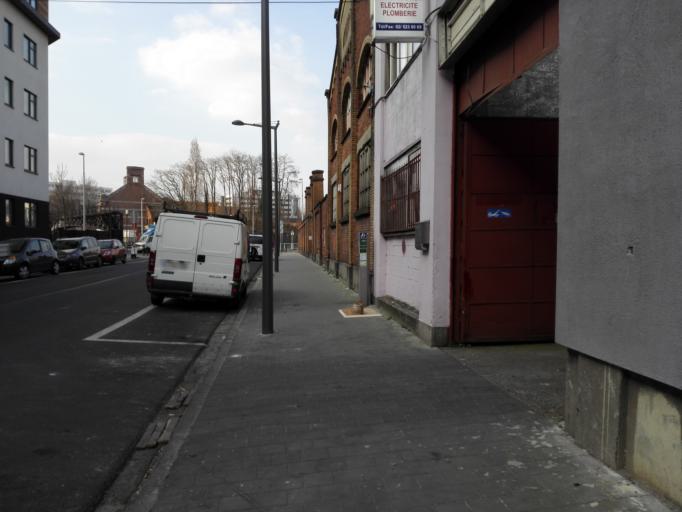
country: BE
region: Brussels Capital
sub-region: Bruxelles-Capitale
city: Brussels
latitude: 50.8410
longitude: 4.3217
